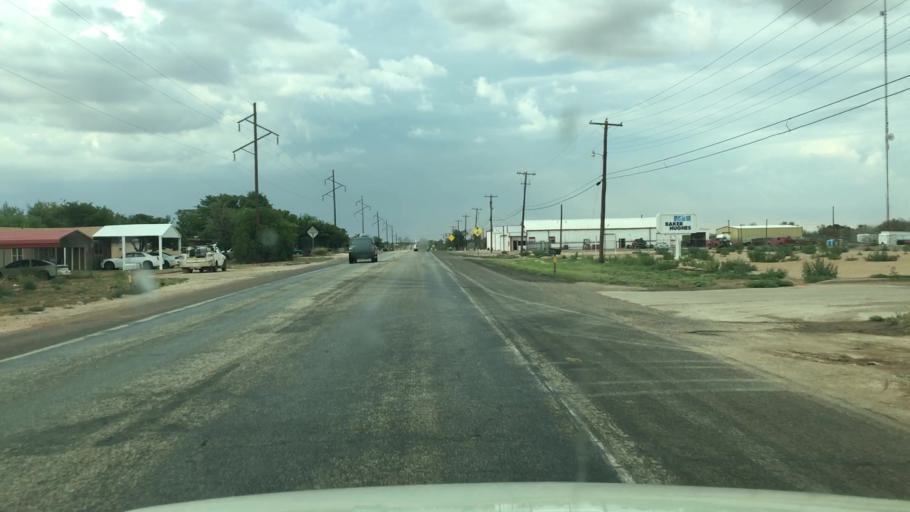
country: US
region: Texas
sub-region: Terry County
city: Brownfield
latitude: 33.1717
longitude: -102.2915
